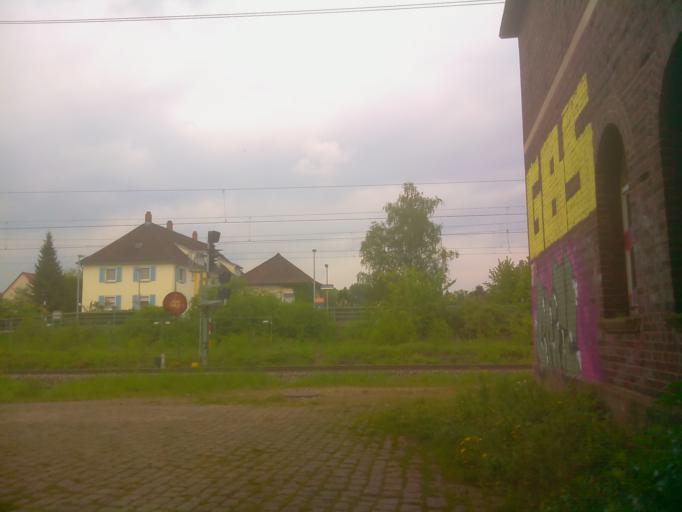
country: DE
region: Baden-Wuerttemberg
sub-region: Karlsruhe Region
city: Eppelheim
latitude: 49.4090
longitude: 8.6523
